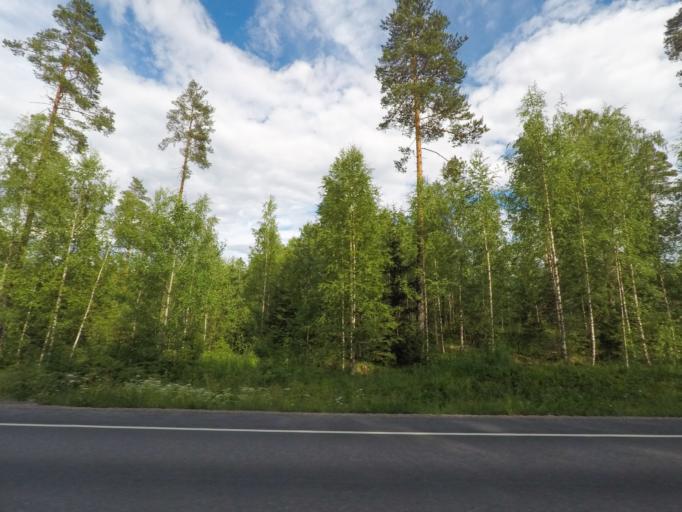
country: FI
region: Uusimaa
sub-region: Porvoo
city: Pukkila
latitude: 60.7821
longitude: 25.4583
